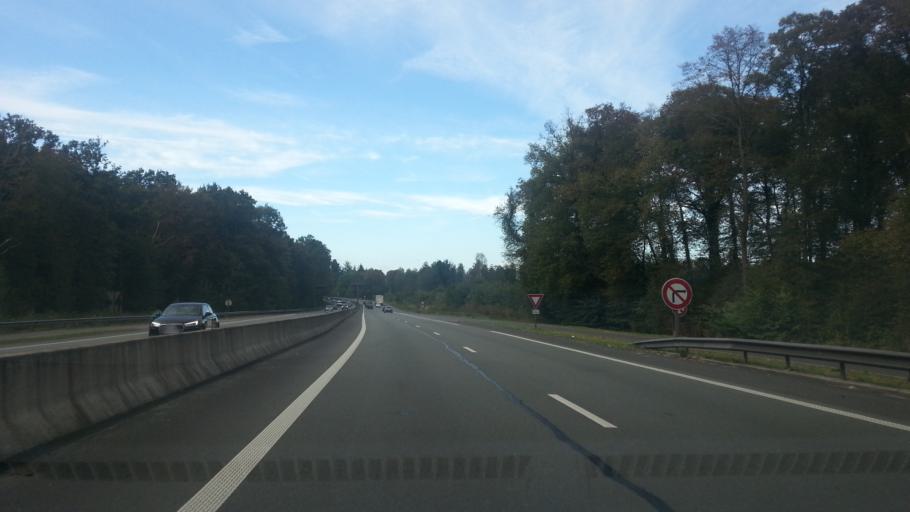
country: FR
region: Picardie
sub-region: Departement de l'Oise
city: Avilly-Saint-Leonard
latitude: 49.2313
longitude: 2.5383
